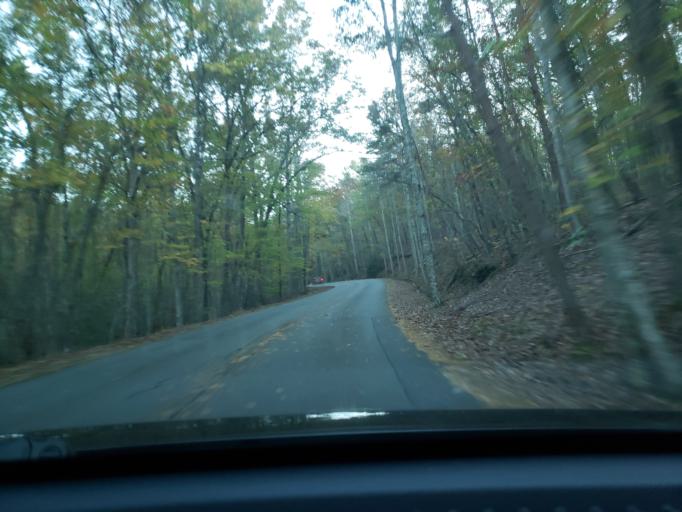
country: US
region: North Carolina
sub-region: Stokes County
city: Danbury
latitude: 36.4098
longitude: -80.2538
